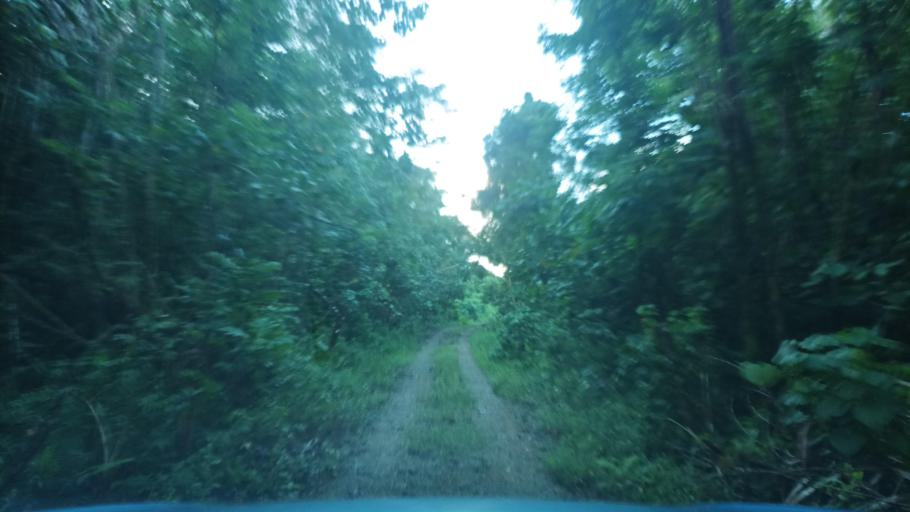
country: FM
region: Pohnpei
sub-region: Kolonia Municipality
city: Kolonia Town
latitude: 6.9707
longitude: 158.1840
